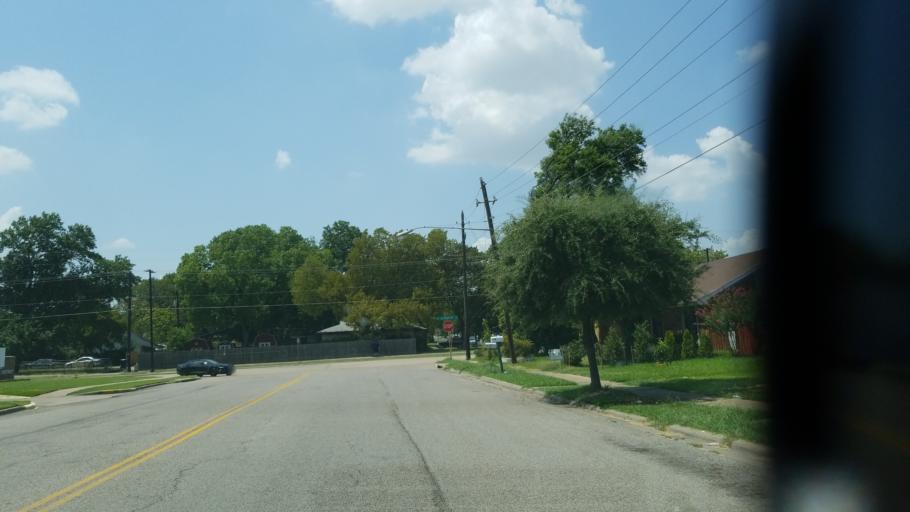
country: US
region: Texas
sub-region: Dallas County
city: Garland
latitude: 32.9267
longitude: -96.6388
